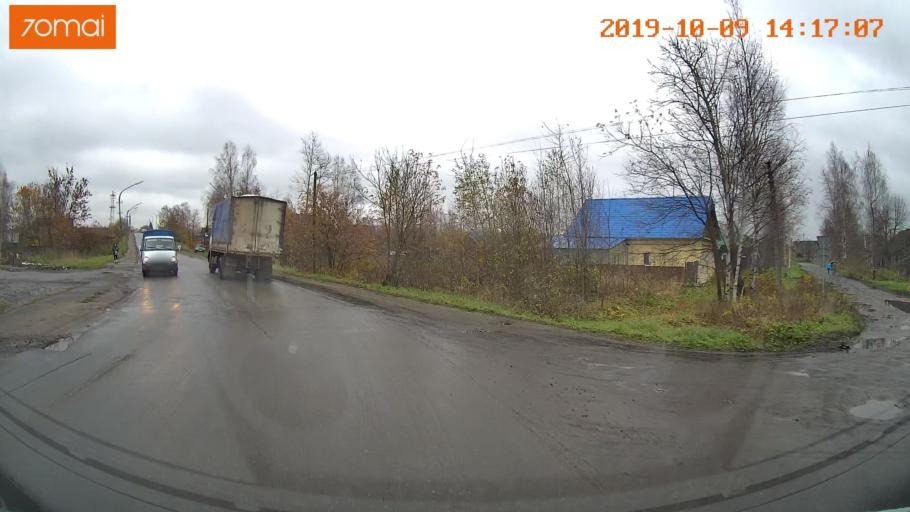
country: RU
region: Kostroma
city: Buy
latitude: 58.4806
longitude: 41.5228
